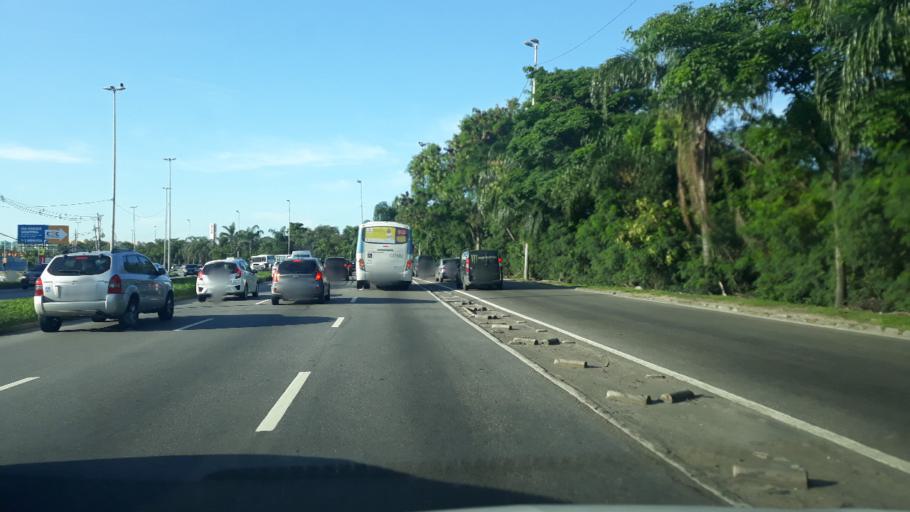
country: BR
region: Rio de Janeiro
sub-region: Sao Joao De Meriti
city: Sao Joao de Meriti
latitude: -22.9584
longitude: -43.3572
